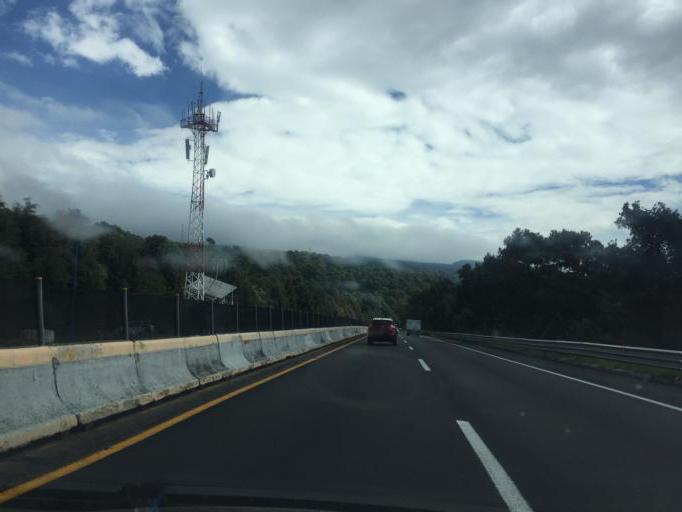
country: MX
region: Morelos
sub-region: Cuernavaca
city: Villa Santiago
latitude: 19.0259
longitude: -99.1859
